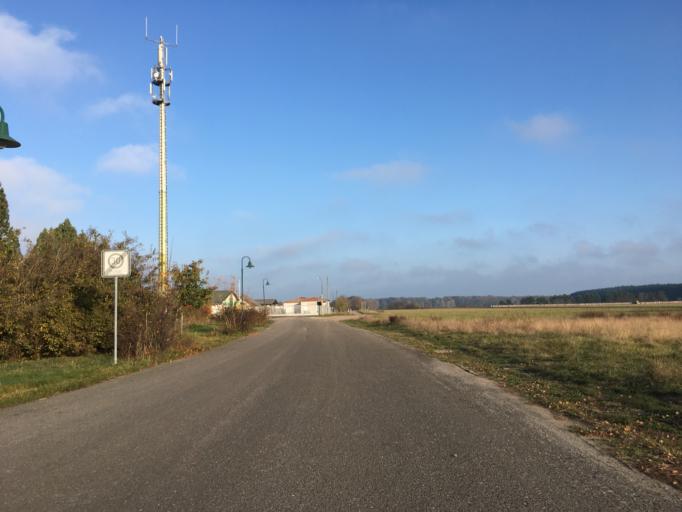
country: DE
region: Brandenburg
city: Schlepzig
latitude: 52.0334
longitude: 13.9042
